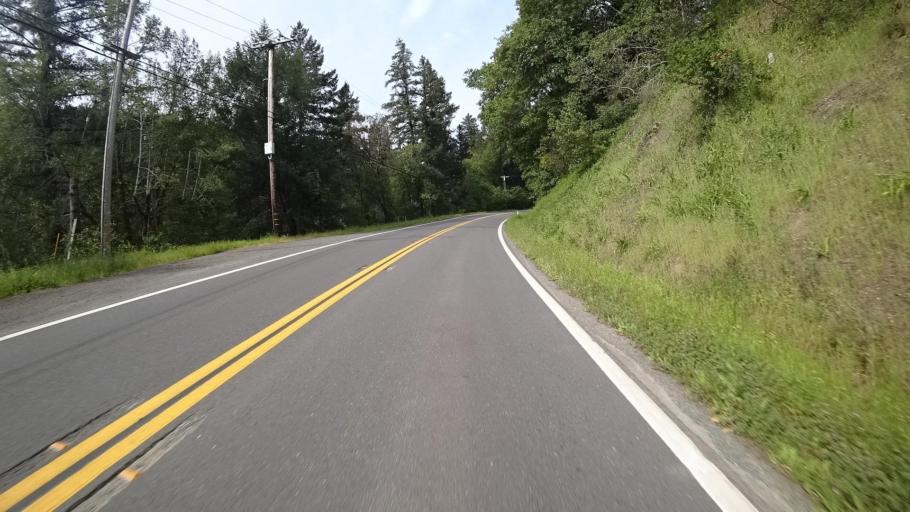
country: US
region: California
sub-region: Humboldt County
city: Redway
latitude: 40.2191
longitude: -123.8095
